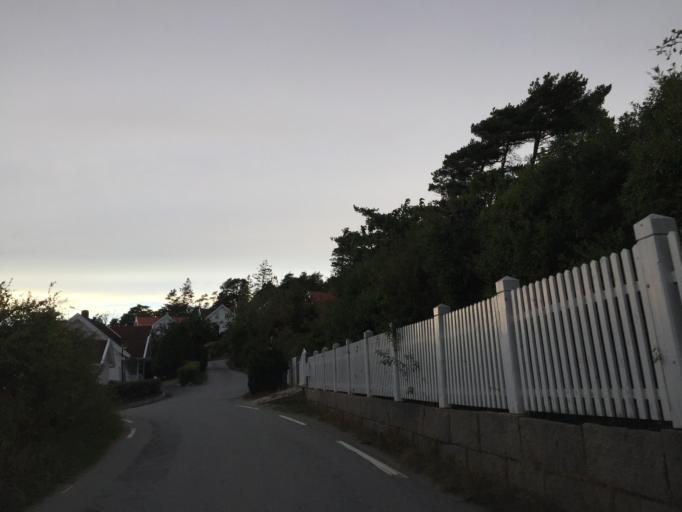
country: NO
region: Ostfold
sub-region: Hvaler
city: Skjaerhalden
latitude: 59.0592
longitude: 11.0059
